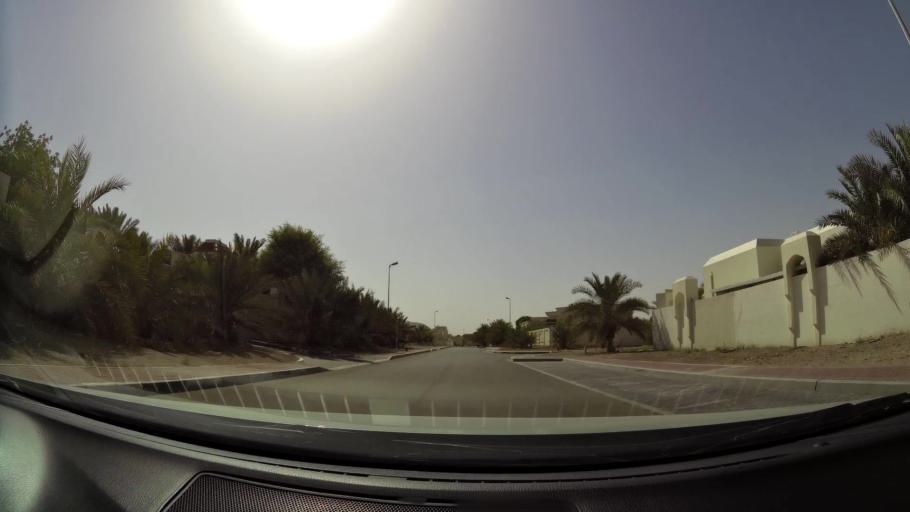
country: OM
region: Al Buraimi
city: Al Buraymi
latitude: 24.3070
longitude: 55.7967
